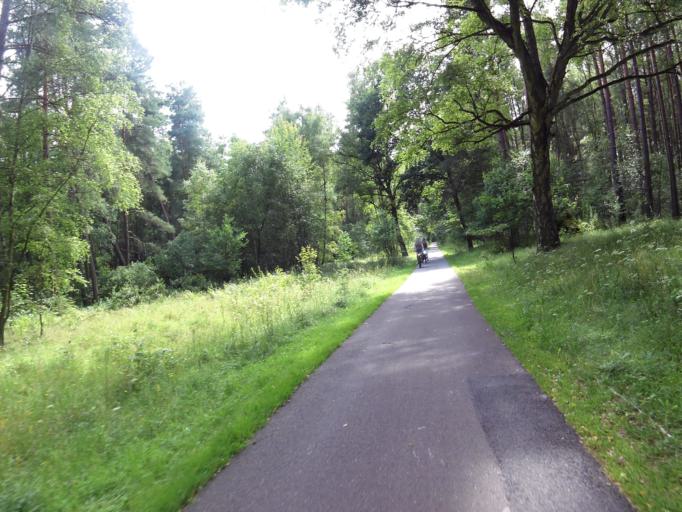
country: DE
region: Brandenburg
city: Lychen
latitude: 53.2385
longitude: 13.2905
